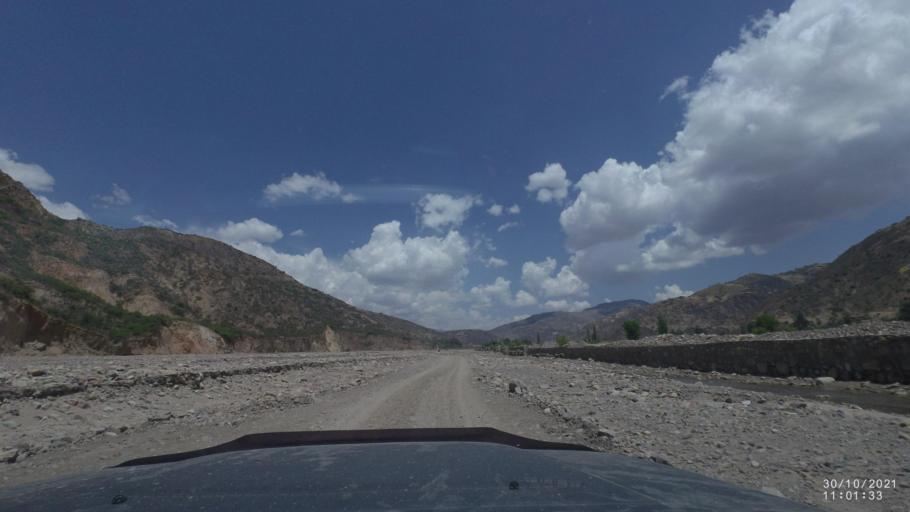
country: BO
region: Cochabamba
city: Sipe Sipe
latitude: -17.5347
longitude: -66.5212
